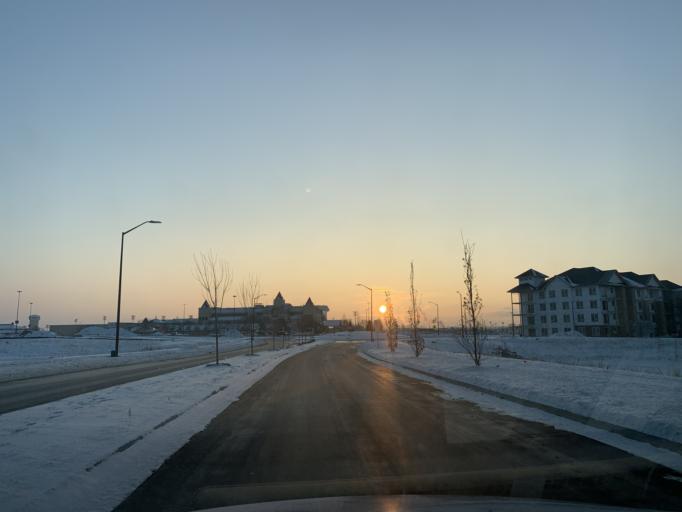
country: US
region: Minnesota
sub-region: Scott County
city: Shakopee
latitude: 44.7924
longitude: -93.4887
